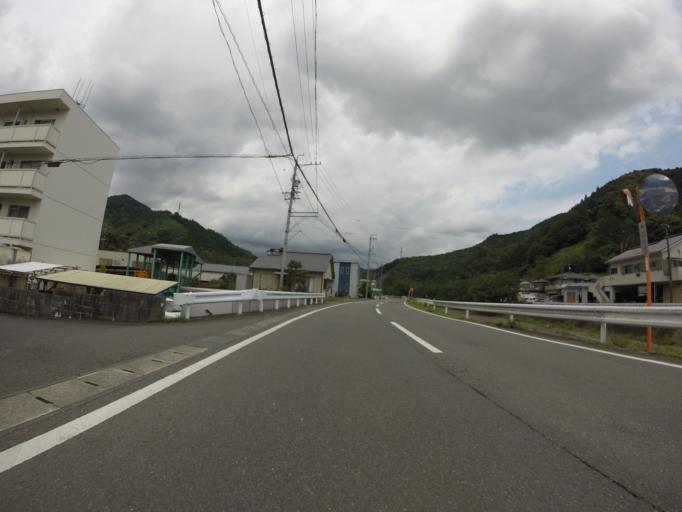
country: JP
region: Shizuoka
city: Shizuoka-shi
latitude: 34.9906
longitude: 138.3066
